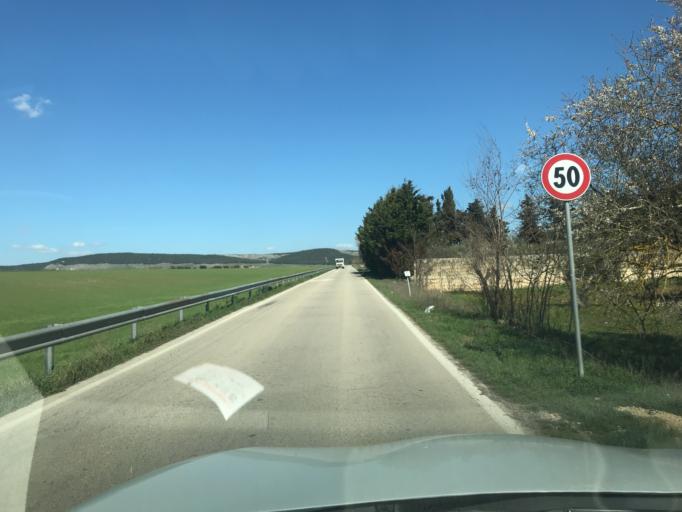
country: IT
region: Apulia
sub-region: Provincia di Bari
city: Gravina in Puglia
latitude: 40.8488
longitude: 16.4277
